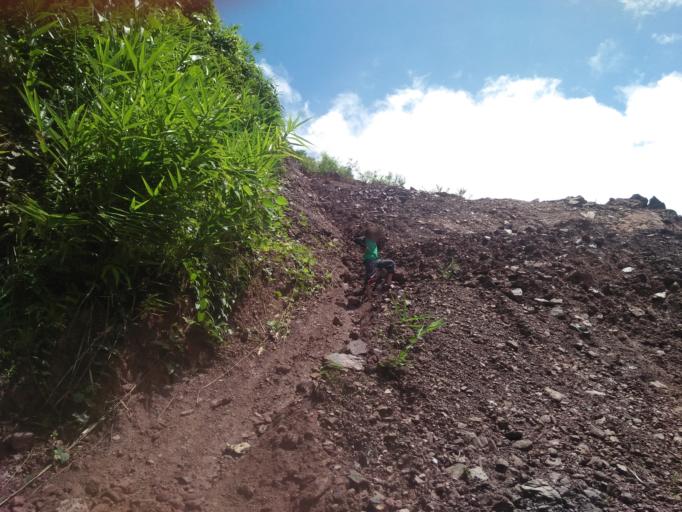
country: TH
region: Nan
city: Chaloem Phra Kiat
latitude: 19.6648
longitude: 100.8986
